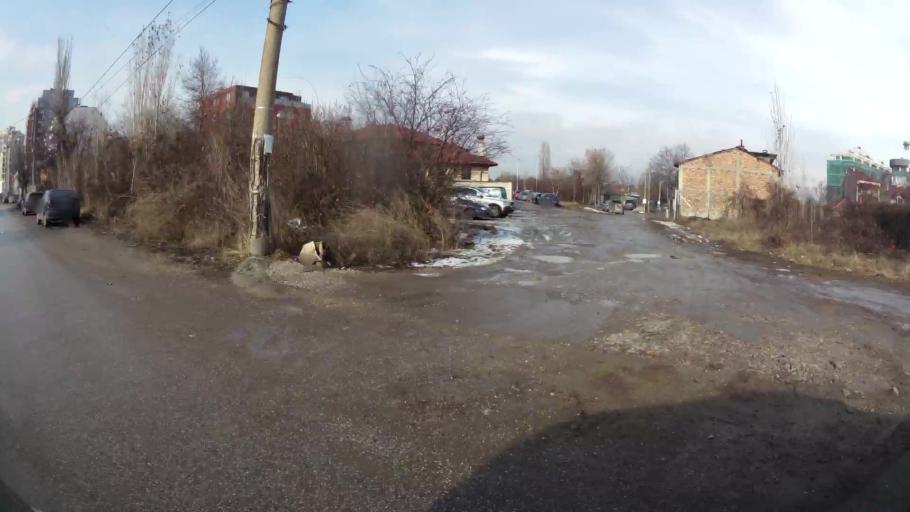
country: BG
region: Sofiya
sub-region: Obshtina Bozhurishte
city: Bozhurishte
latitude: 42.7242
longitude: 23.2614
